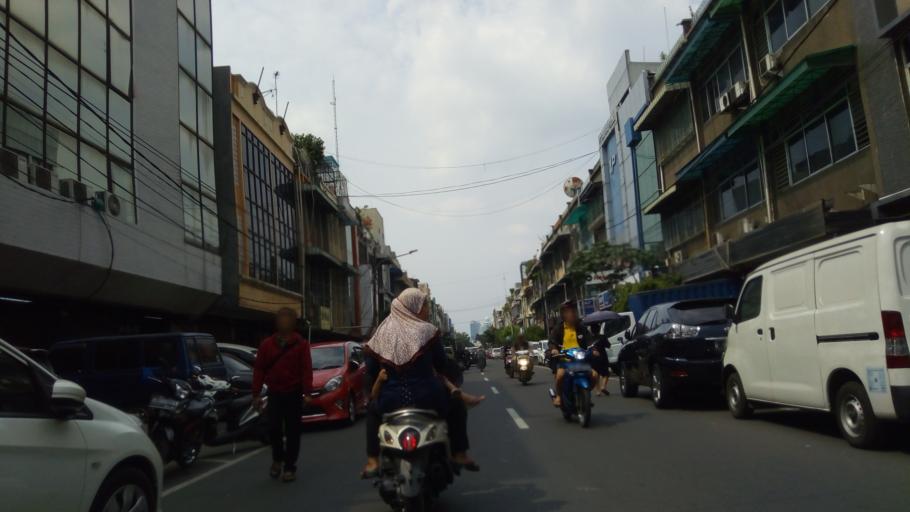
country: ID
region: Jakarta Raya
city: Jakarta
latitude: -6.1597
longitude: 106.8278
